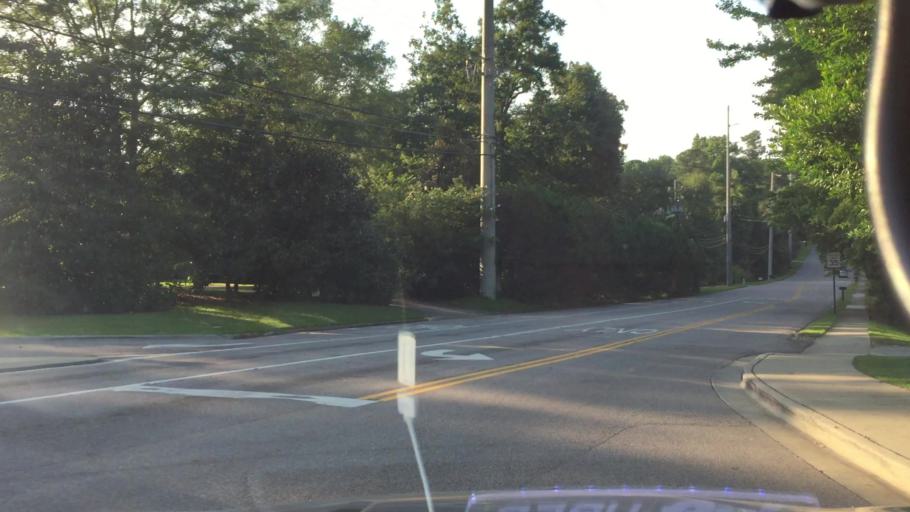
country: US
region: Alabama
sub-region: Lee County
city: Auburn
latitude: 32.5918
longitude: -85.4647
